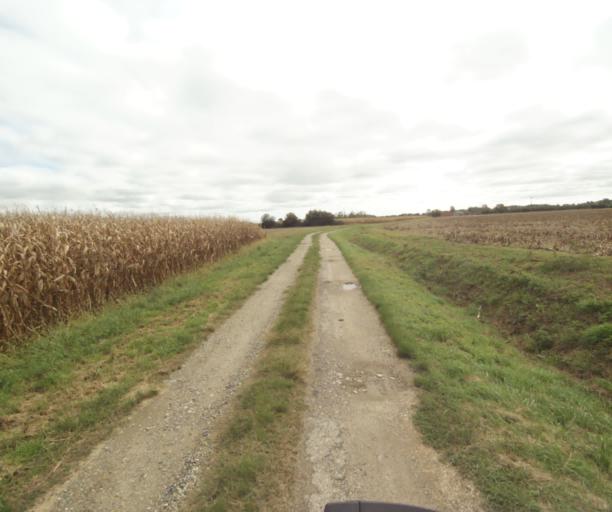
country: FR
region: Midi-Pyrenees
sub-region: Departement du Tarn-et-Garonne
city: Montech
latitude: 43.9712
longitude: 1.2008
